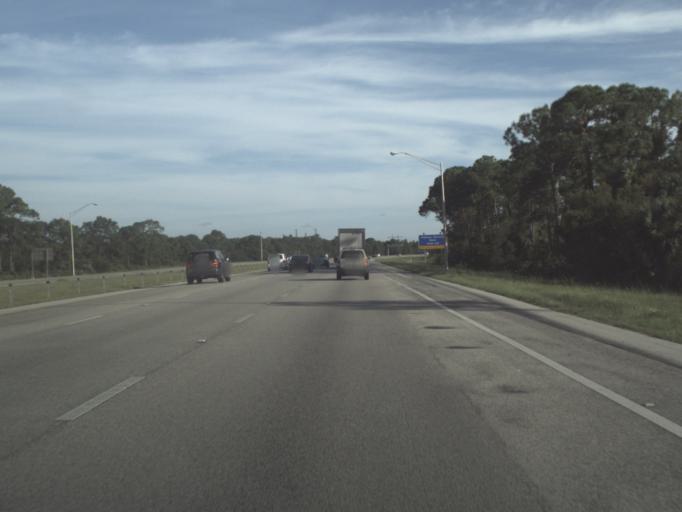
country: US
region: Florida
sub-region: Charlotte County
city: Charlotte Park
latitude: 26.8731
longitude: -81.9788
